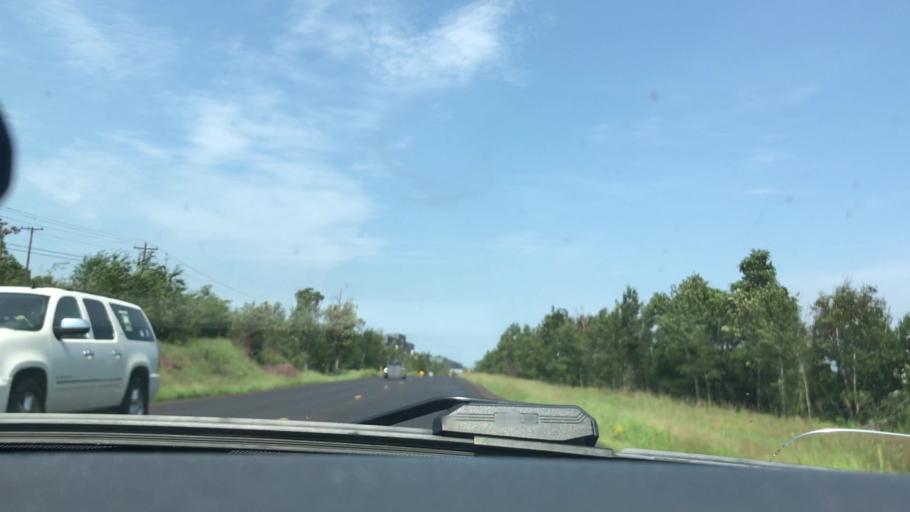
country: US
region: Minnesota
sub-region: Lake County
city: Silver Bay
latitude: 47.2832
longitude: -91.2686
